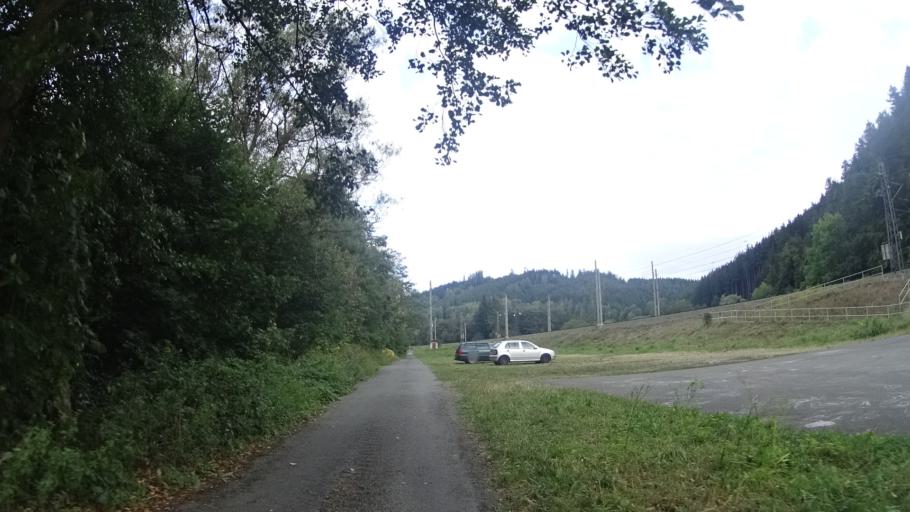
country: CZ
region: Olomoucky
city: Zabreh
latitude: 49.8640
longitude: 16.8093
